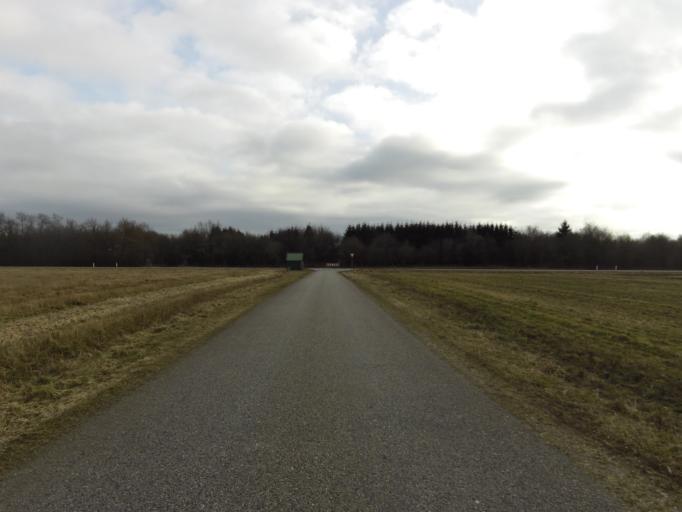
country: DK
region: South Denmark
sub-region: Tonder Kommune
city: Toftlund
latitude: 55.2014
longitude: 9.1814
